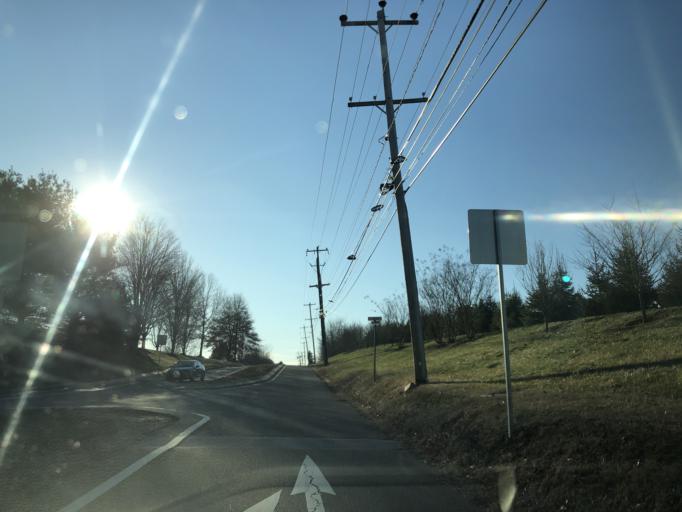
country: US
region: Pennsylvania
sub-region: Delaware County
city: Chester Heights
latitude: 39.8798
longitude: -75.5212
